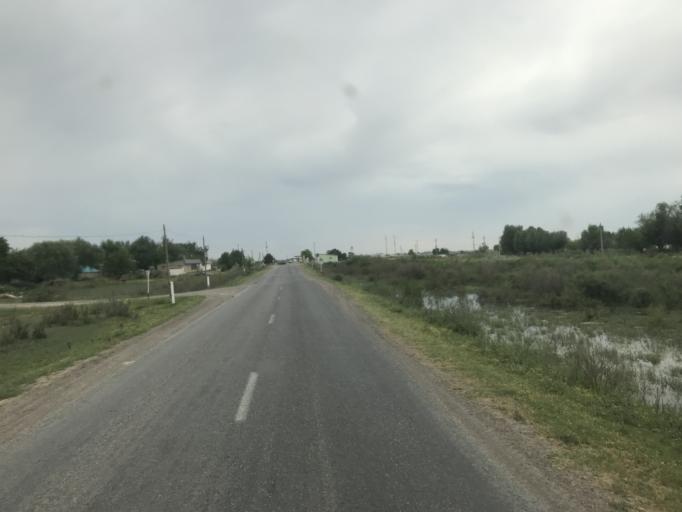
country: KZ
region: Ongtustik Qazaqstan
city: Asykata
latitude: 40.9132
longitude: 68.3943
